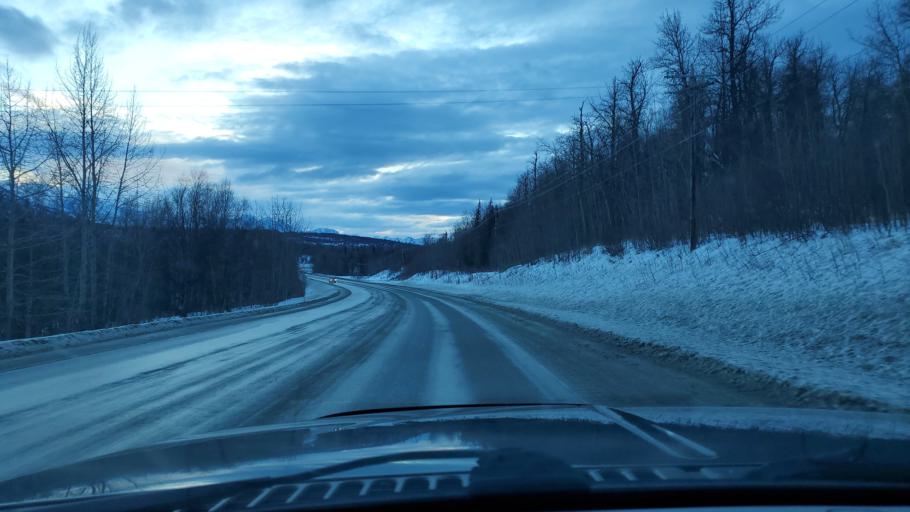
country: US
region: Alaska
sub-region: Matanuska-Susitna Borough
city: Lazy Mountain
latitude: 61.6863
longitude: -148.9849
